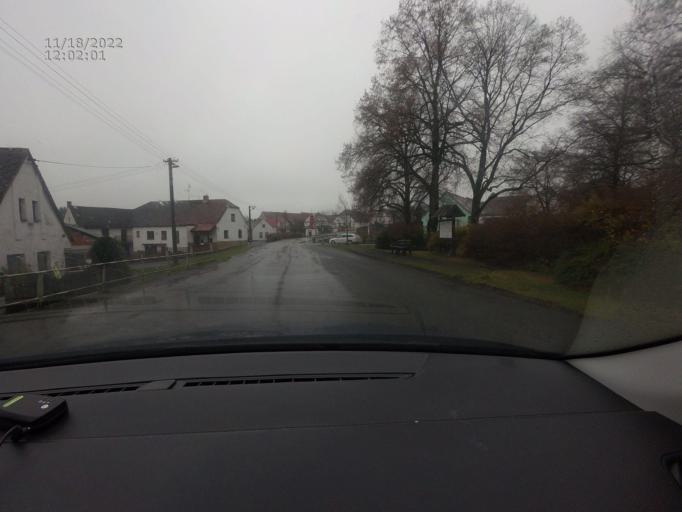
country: CZ
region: Plzensky
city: St'ahlavy
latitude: 49.6556
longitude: 13.4783
